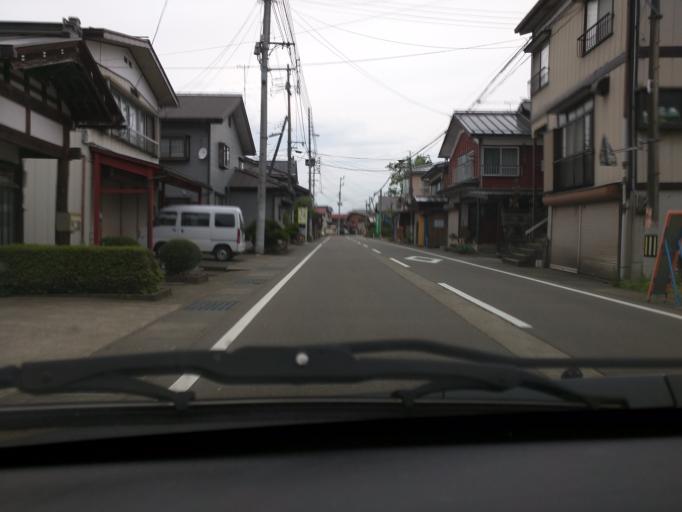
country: JP
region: Niigata
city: Muikamachi
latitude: 37.1985
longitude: 138.9515
